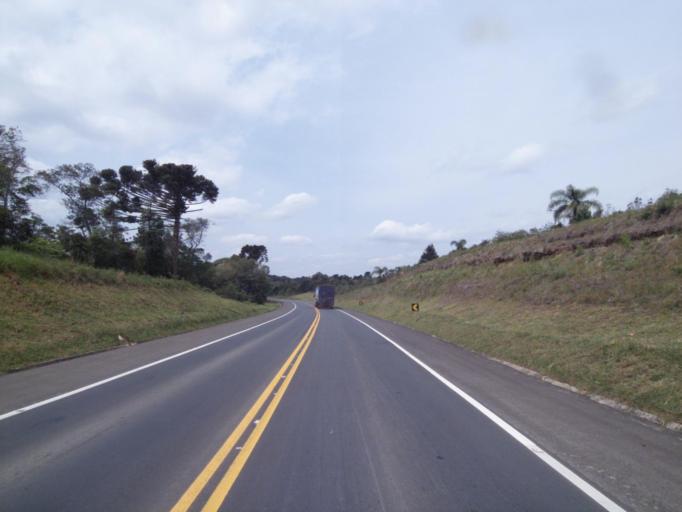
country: BR
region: Parana
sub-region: Irati
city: Irati
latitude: -25.4727
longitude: -50.4885
